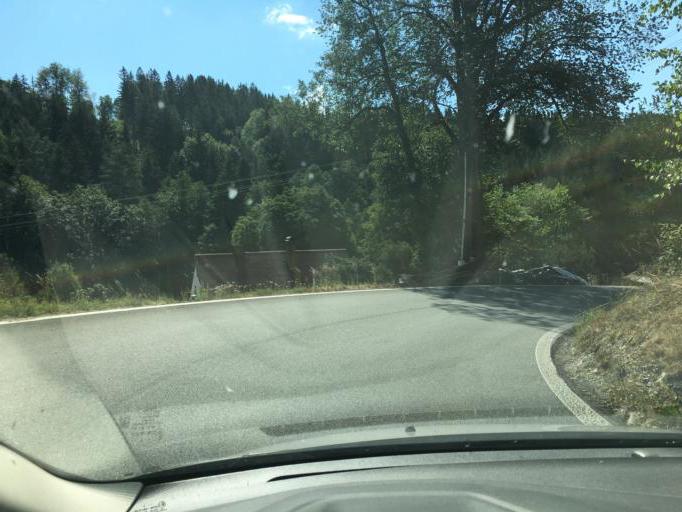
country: CZ
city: Plavy
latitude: 50.7024
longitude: 15.3319
